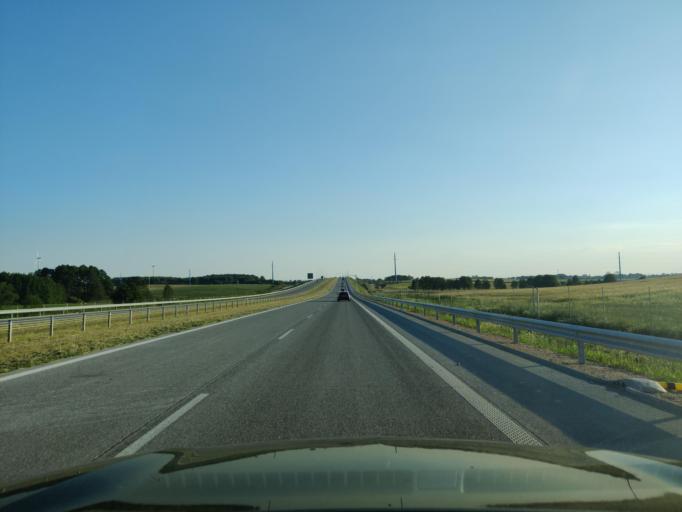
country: PL
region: Masovian Voivodeship
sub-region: Powiat mlawski
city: Mlawa
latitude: 53.0794
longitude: 20.3889
